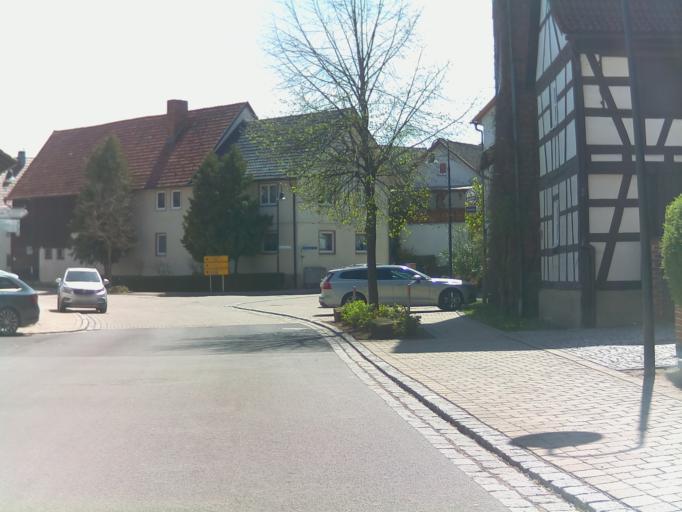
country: DE
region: Thuringia
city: Veilsdorf
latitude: 50.3083
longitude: 10.8044
